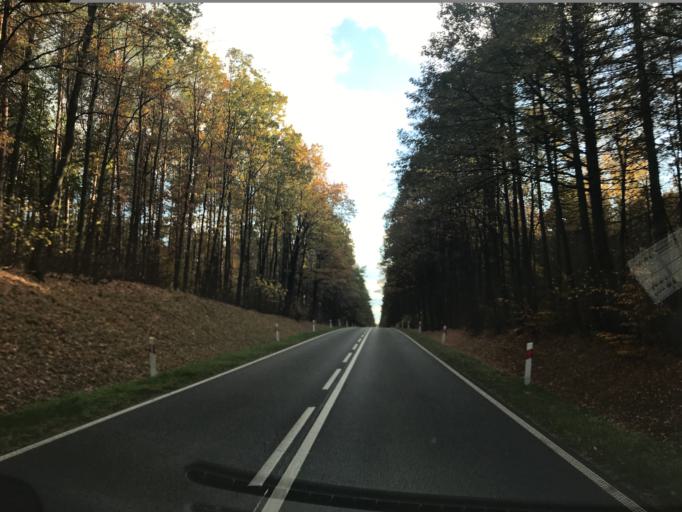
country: PL
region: Warmian-Masurian Voivodeship
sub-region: Powiat dzialdowski
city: Lidzbark
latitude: 53.3306
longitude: 19.8173
